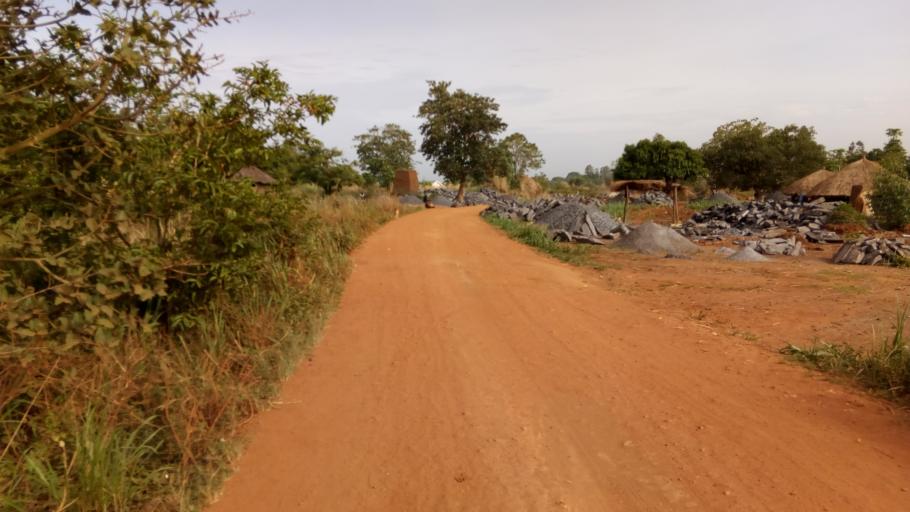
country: UG
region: Northern Region
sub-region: Gulu District
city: Gulu
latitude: 2.7936
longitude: 32.3240
